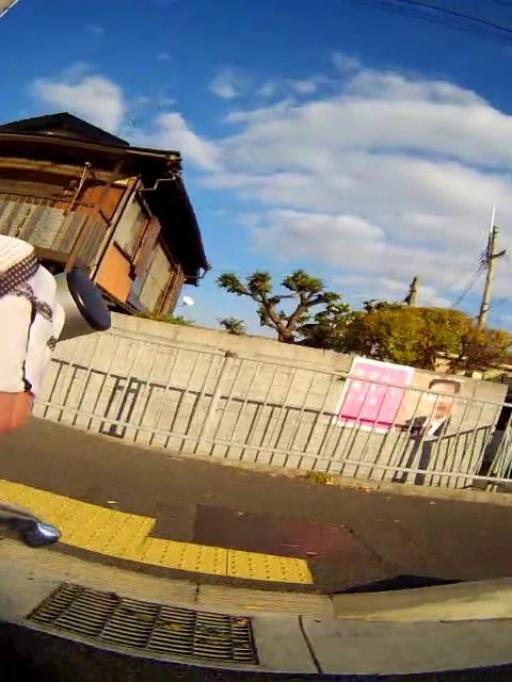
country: JP
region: Hyogo
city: Itami
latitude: 34.7633
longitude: 135.4116
